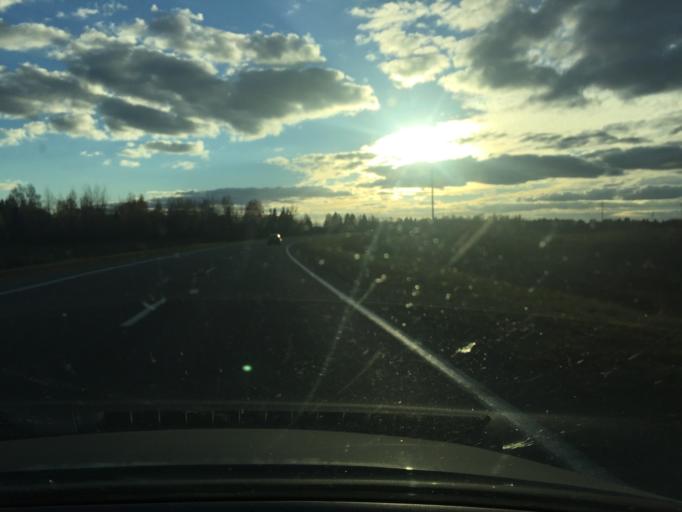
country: BY
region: Vitebsk
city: Vyerkhnyadzvinsk
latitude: 55.8294
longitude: 27.8172
